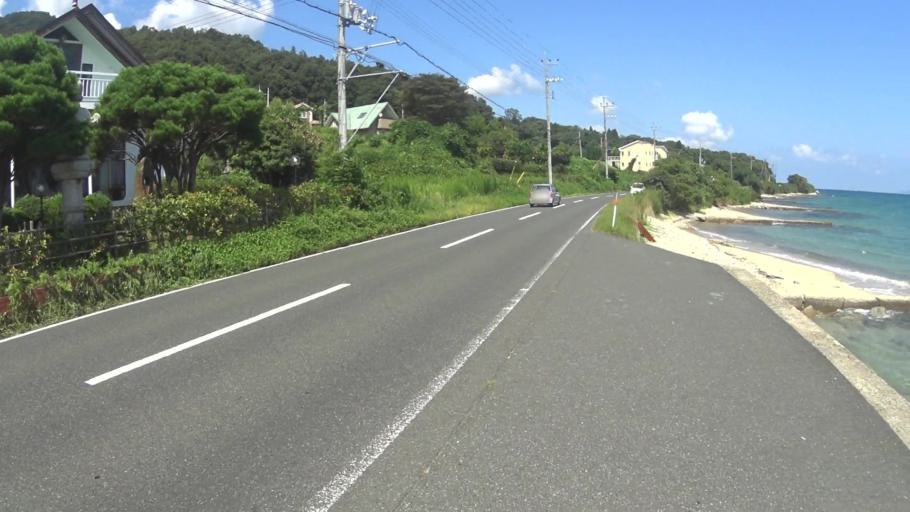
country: JP
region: Kyoto
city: Miyazu
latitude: 35.5913
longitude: 135.2089
